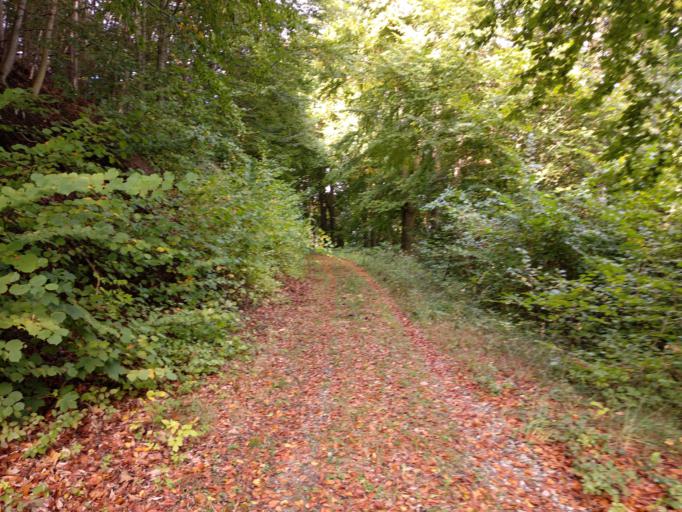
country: DE
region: North Rhine-Westphalia
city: Beverungen
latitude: 51.6471
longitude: 9.3714
